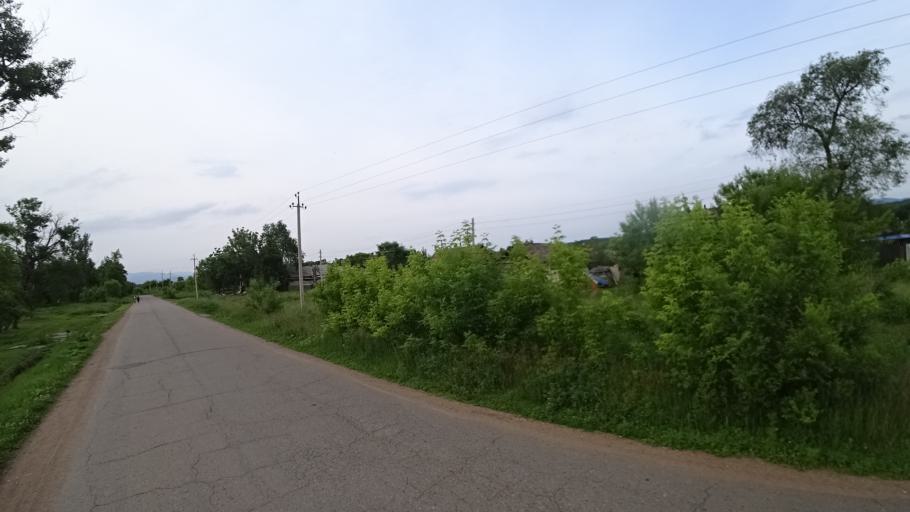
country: RU
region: Primorskiy
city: Novosysoyevka
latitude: 44.2418
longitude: 133.3679
